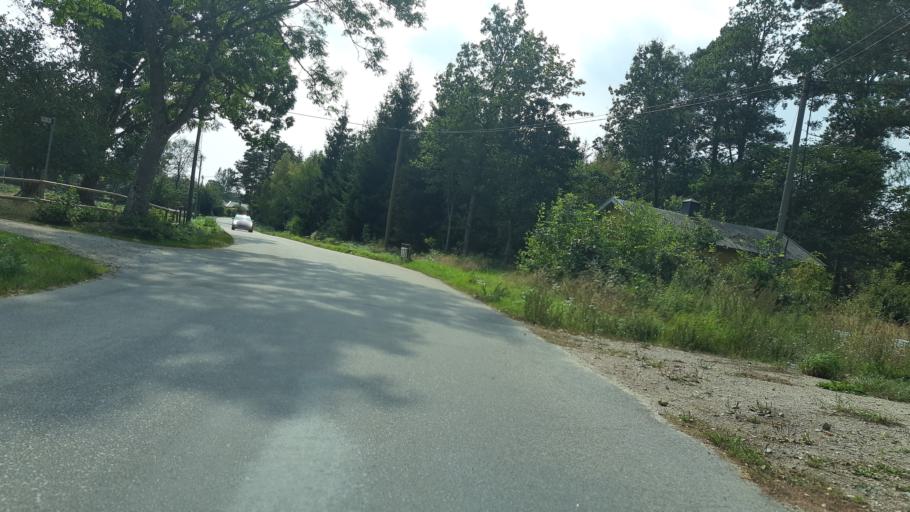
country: SE
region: Blekinge
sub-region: Karlskrona Kommun
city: Nattraby
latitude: 56.1840
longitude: 15.4986
